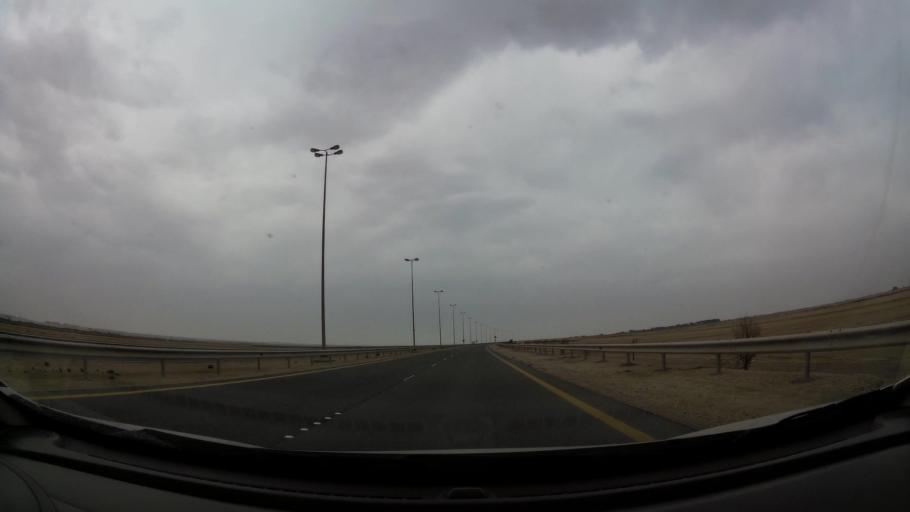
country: BH
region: Central Governorate
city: Dar Kulayb
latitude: 26.0078
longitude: 50.4842
